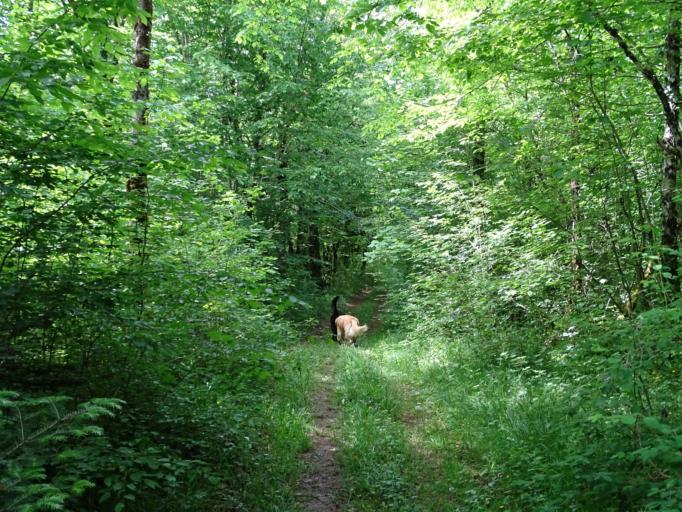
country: FR
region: Franche-Comte
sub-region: Departement du Doubs
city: Levier
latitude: 47.0152
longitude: 6.0003
